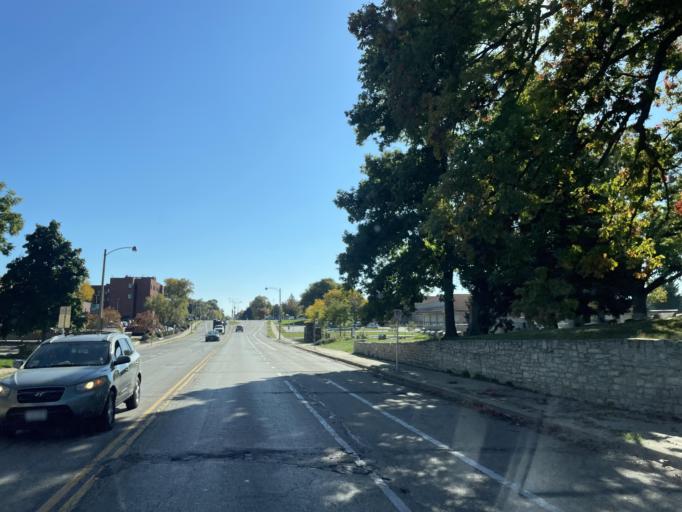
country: US
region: Wisconsin
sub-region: Milwaukee County
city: Wauwatosa
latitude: 43.0632
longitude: -88.0075
